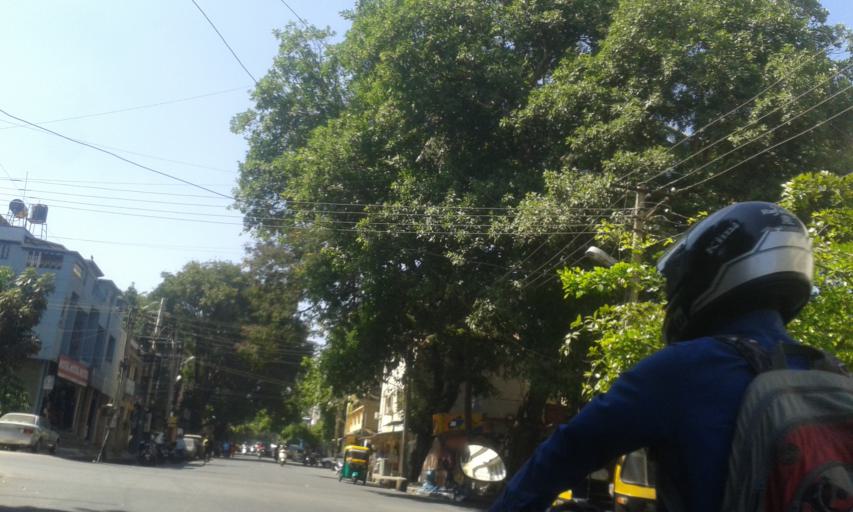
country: IN
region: Karnataka
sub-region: Bangalore Urban
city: Bangalore
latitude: 12.9189
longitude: 77.5954
